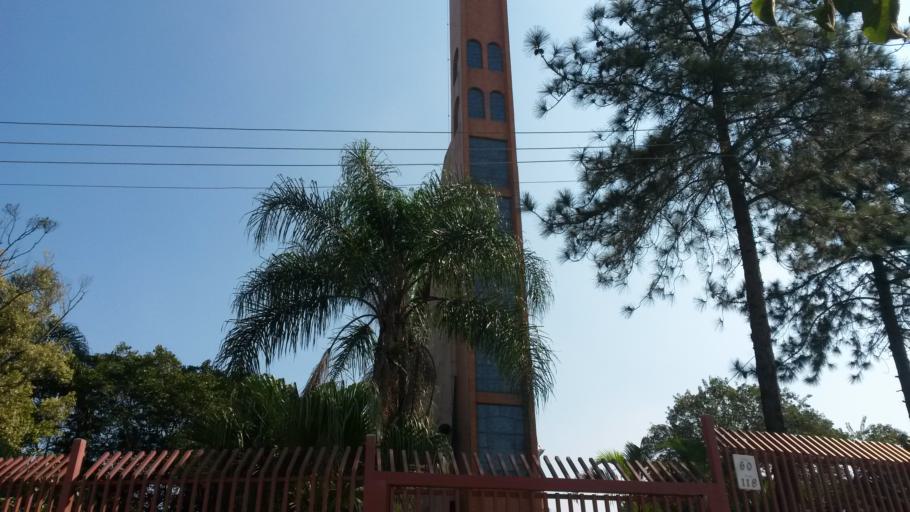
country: BR
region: Sao Paulo
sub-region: Sao Bernardo Do Campo
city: Sao Bernardo do Campo
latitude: -23.6923
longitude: -46.5827
